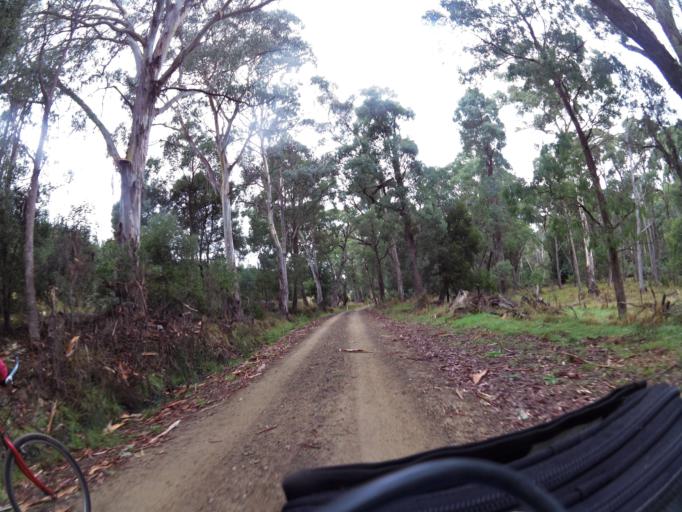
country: AU
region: New South Wales
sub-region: Greater Hume Shire
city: Holbrook
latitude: -36.1685
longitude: 147.4958
